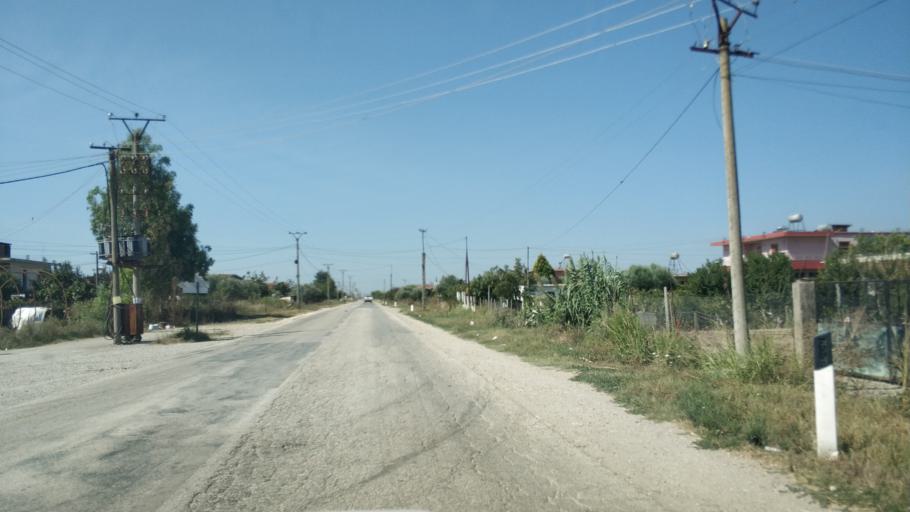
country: AL
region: Tirane
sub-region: Rrethi i Kavajes
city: Rrogozhine
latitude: 41.0518
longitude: 19.6472
